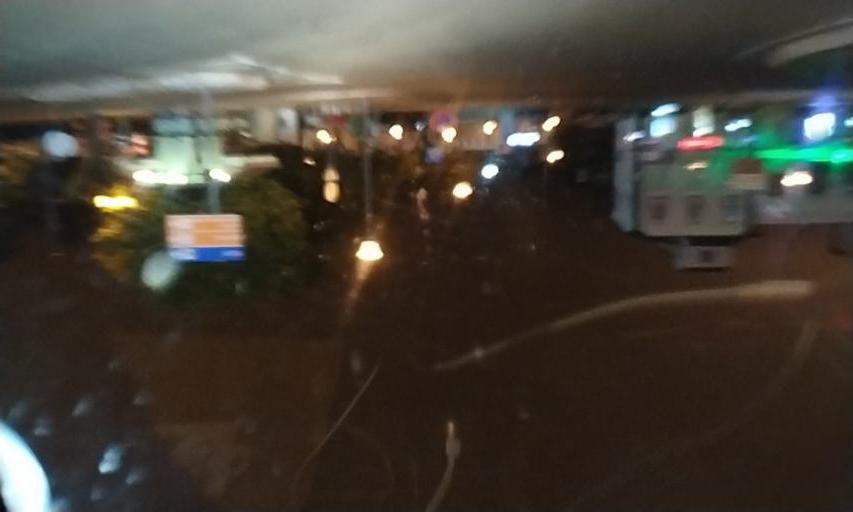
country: PT
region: Evora
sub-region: Estremoz
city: Estremoz
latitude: 38.8435
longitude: -7.5868
